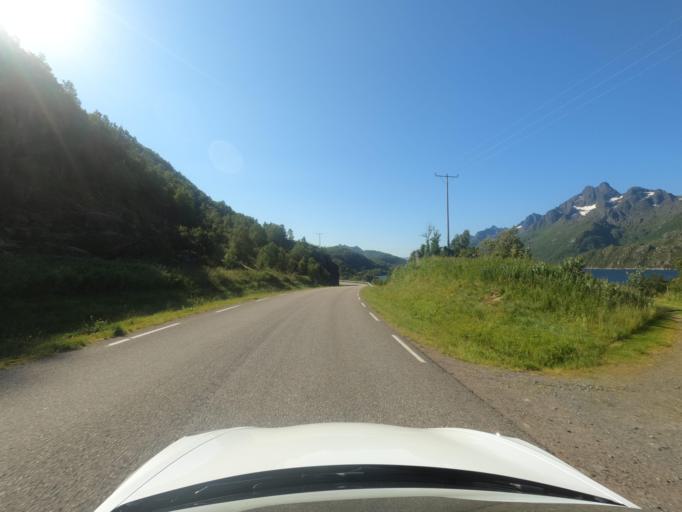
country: NO
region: Nordland
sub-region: Hadsel
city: Stokmarknes
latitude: 68.4497
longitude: 15.2042
